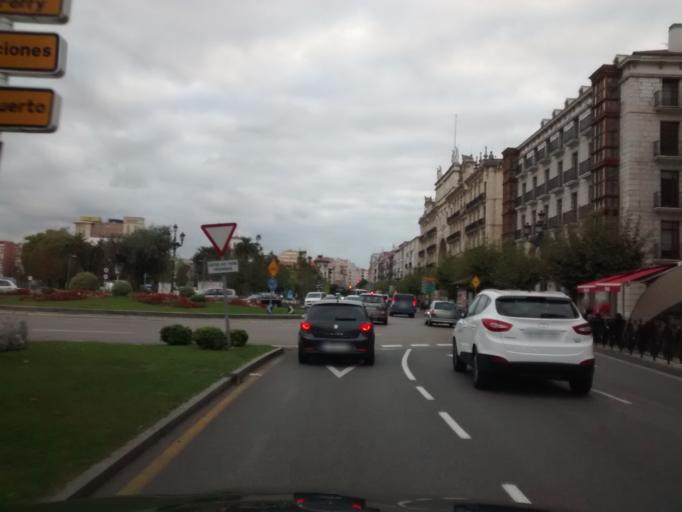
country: ES
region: Cantabria
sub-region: Provincia de Cantabria
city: Santander
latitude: 43.4620
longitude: -3.8018
